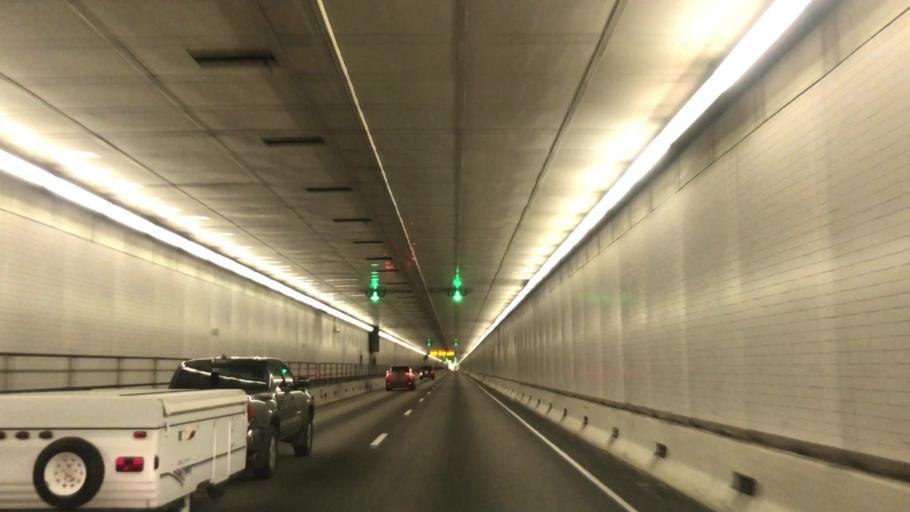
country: US
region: Colorado
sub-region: Summit County
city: Keystone
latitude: 39.6790
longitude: -105.9229
